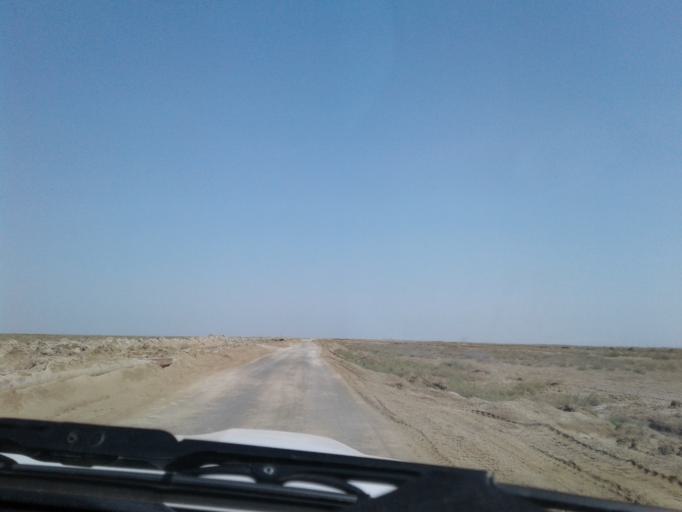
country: IR
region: Golestan
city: Gomishan
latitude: 37.8255
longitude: 53.9215
